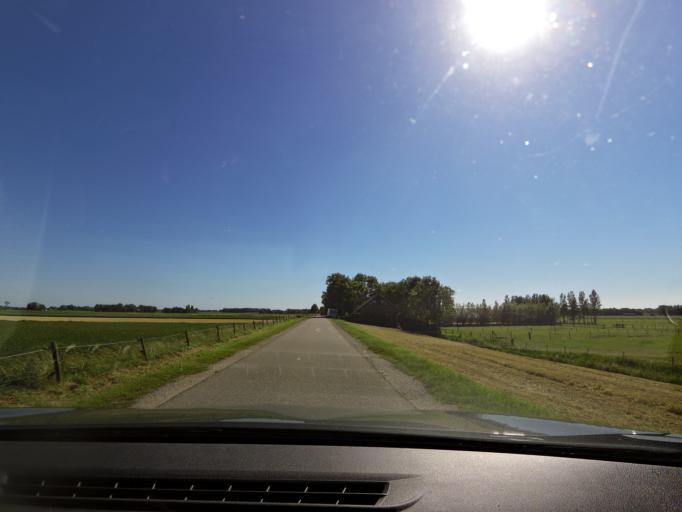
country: NL
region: South Holland
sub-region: Gemeente Hellevoetsluis
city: Nieuw-Helvoet
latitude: 51.8490
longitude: 4.1074
